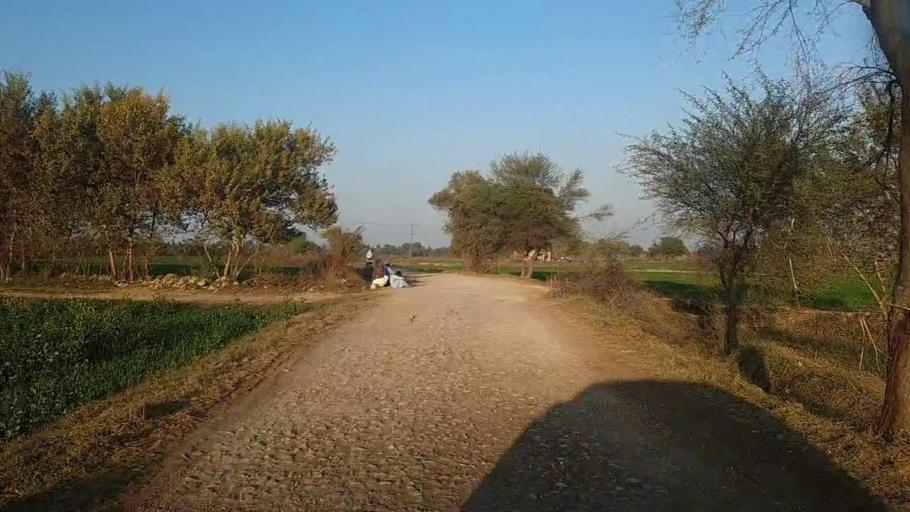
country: PK
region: Sindh
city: Mirpur Mathelo
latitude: 27.8806
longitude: 69.6511
